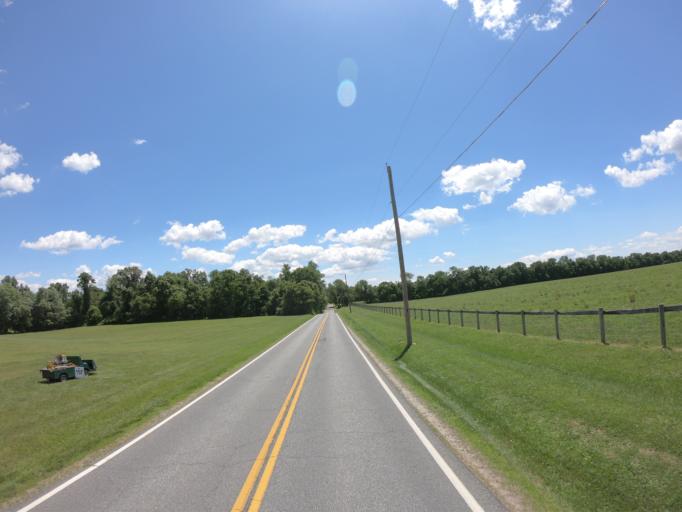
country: US
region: Delaware
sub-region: New Castle County
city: Middletown
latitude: 39.4717
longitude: -75.7792
